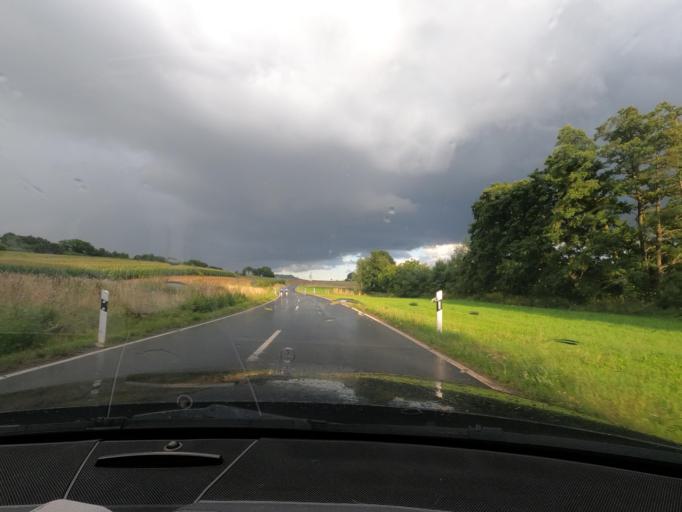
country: DE
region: Hesse
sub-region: Regierungsbezirk Kassel
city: Wolfhagen
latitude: 51.3282
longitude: 9.2291
